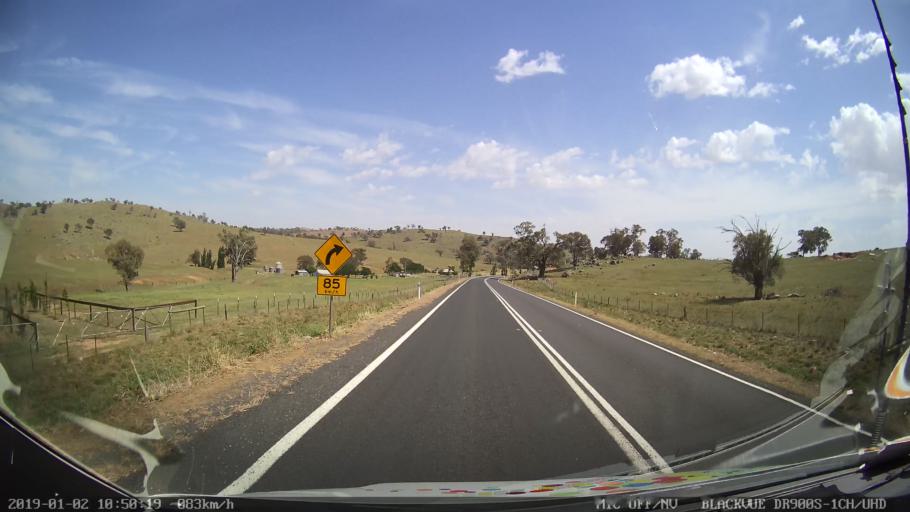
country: AU
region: New South Wales
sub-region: Cootamundra
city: Cootamundra
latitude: -34.7153
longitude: 148.2766
